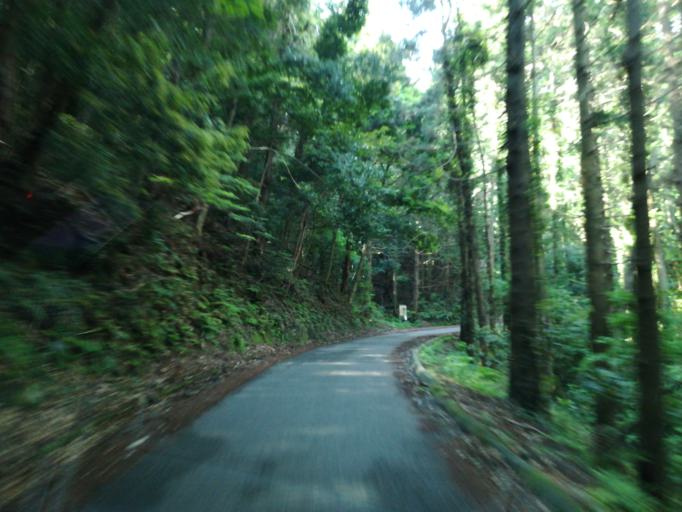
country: JP
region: Ibaraki
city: Tsukuba
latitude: 36.1846
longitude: 140.1182
